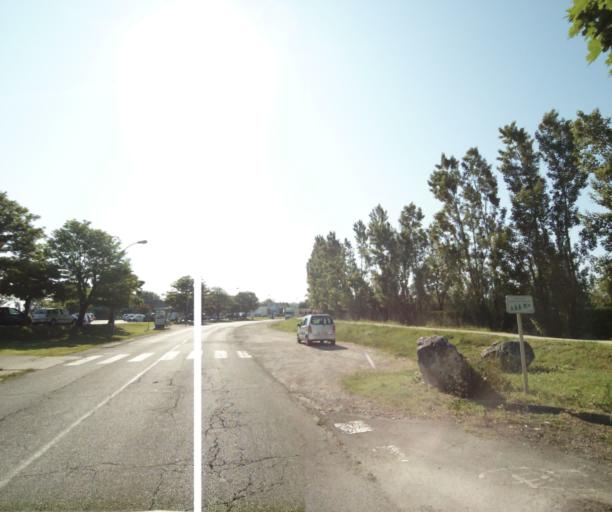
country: FR
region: Midi-Pyrenees
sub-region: Departement du Tarn-et-Garonne
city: Montauban
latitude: 44.0218
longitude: 1.3788
